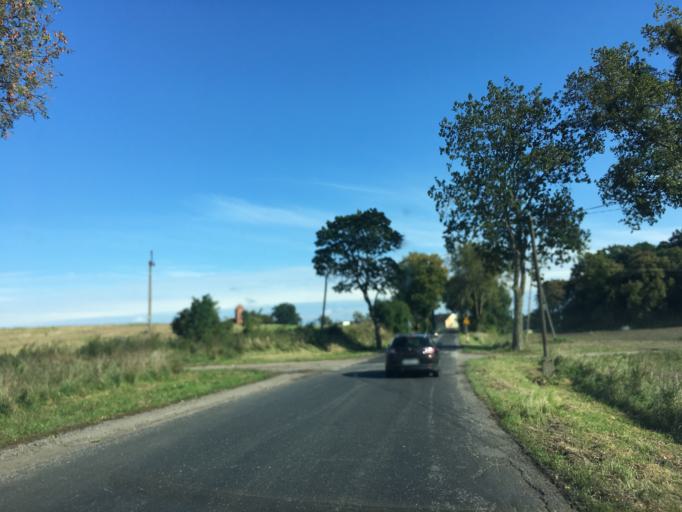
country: PL
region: Kujawsko-Pomorskie
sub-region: Powiat swiecki
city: Warlubie
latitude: 53.5958
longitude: 18.5909
